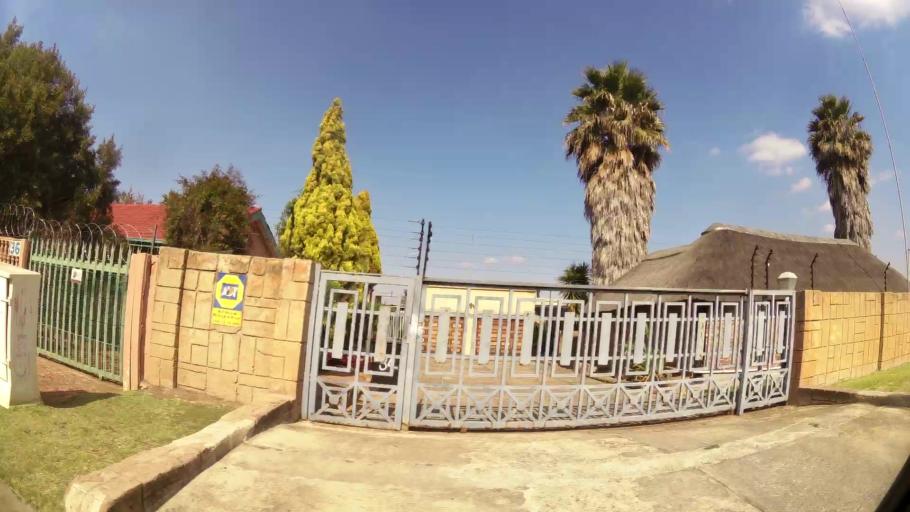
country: ZA
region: Gauteng
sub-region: Ekurhuleni Metropolitan Municipality
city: Boksburg
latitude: -26.1904
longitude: 28.2156
